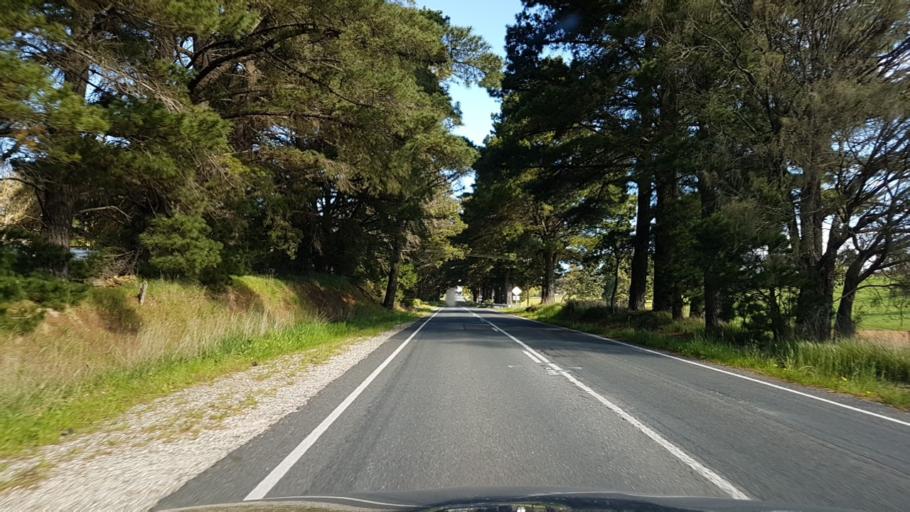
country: AU
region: South Australia
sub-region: Adelaide Hills
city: Lobethal
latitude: -34.8734
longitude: 138.8896
